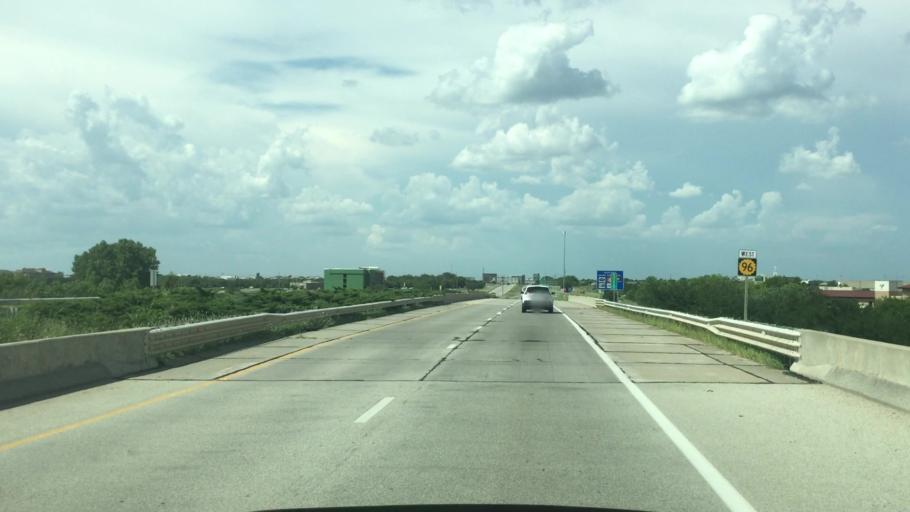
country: US
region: Kansas
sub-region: Butler County
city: Andover
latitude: 37.7159
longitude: -97.1995
